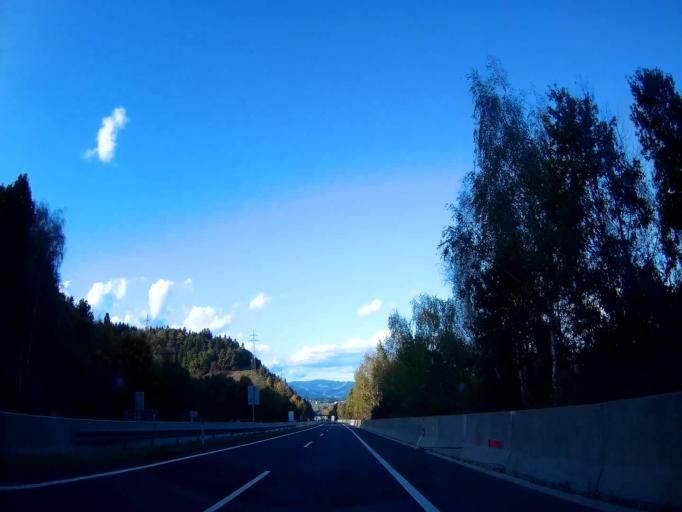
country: AT
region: Carinthia
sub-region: Politischer Bezirk Wolfsberg
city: Sankt Andrae
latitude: 46.7575
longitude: 14.8158
